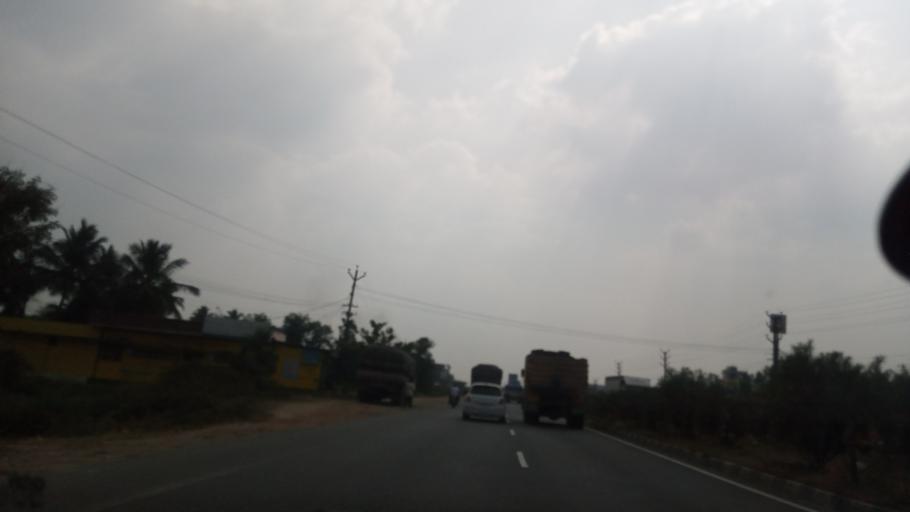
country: IN
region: Tamil Nadu
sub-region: Salem
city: Omalur
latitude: 11.7766
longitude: 78.0565
